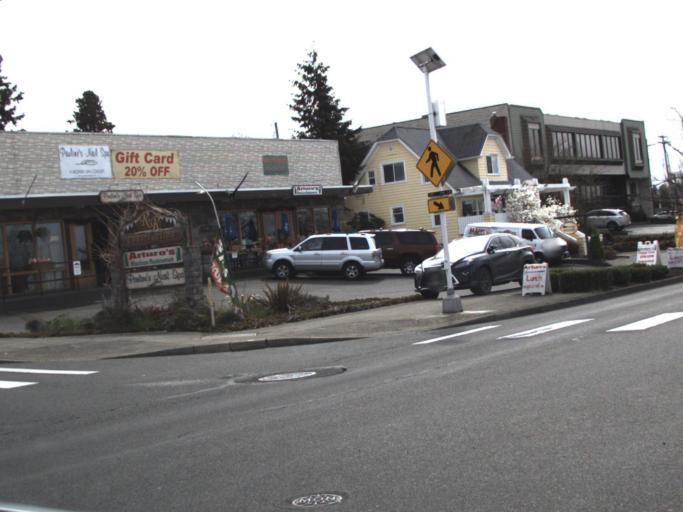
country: US
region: Washington
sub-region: King County
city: Des Moines
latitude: 47.4030
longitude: -122.3246
